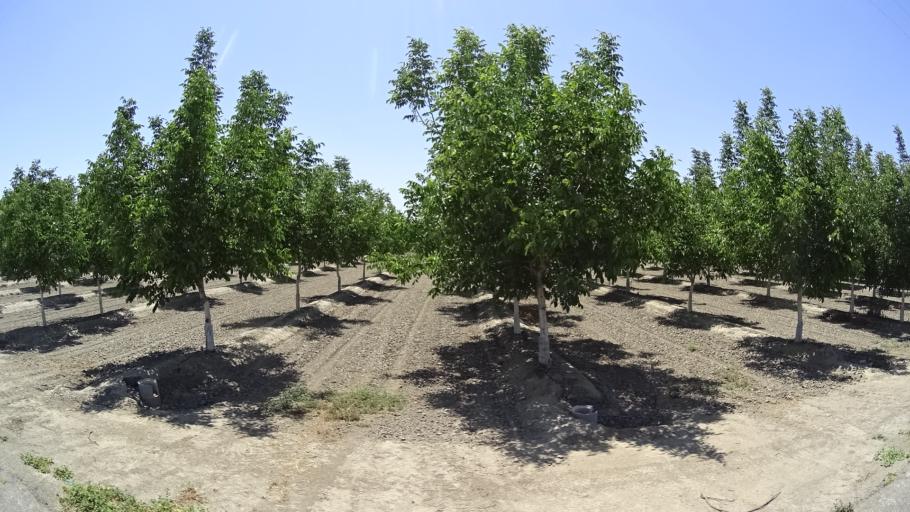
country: US
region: California
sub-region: Fresno County
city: Laton
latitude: 36.3864
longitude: -119.7404
